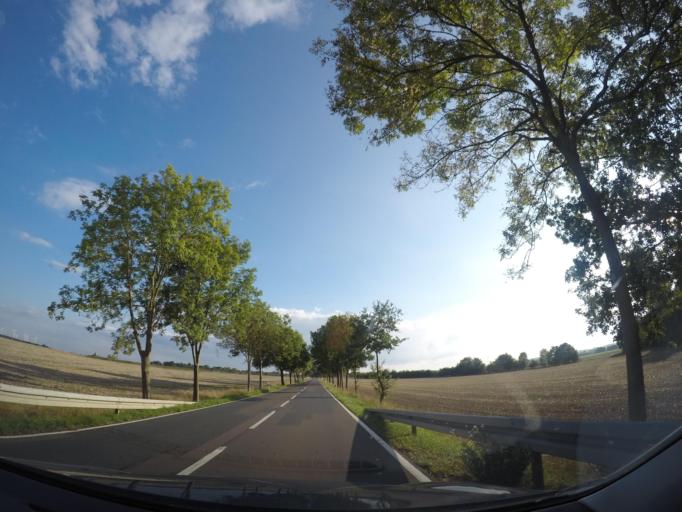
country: DE
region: Saxony-Anhalt
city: Weferlingen
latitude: 52.3558
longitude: 11.0790
